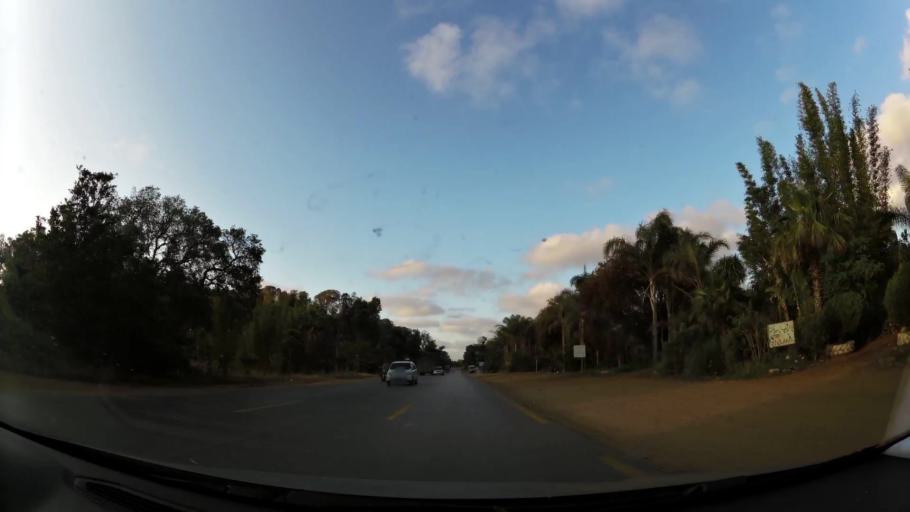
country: MA
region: Gharb-Chrarda-Beni Hssen
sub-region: Kenitra Province
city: Kenitra
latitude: 34.2140
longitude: -6.6681
